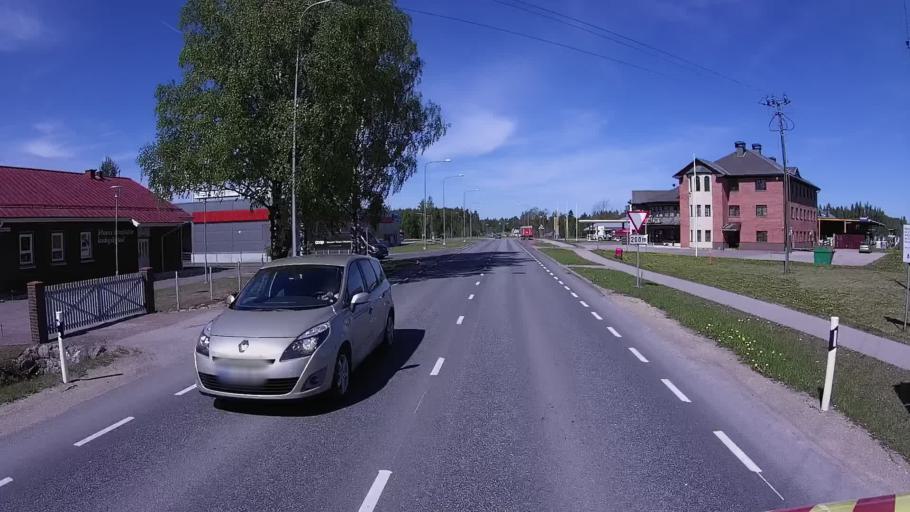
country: EE
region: Polvamaa
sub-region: Polva linn
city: Polva
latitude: 58.0662
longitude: 27.0776
